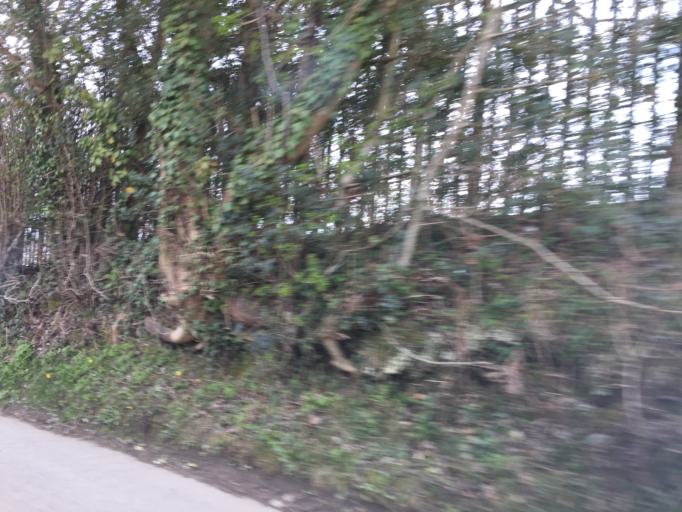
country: GB
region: Wales
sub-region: Caerphilly County Borough
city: Bedwas
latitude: 51.5945
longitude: -3.2153
